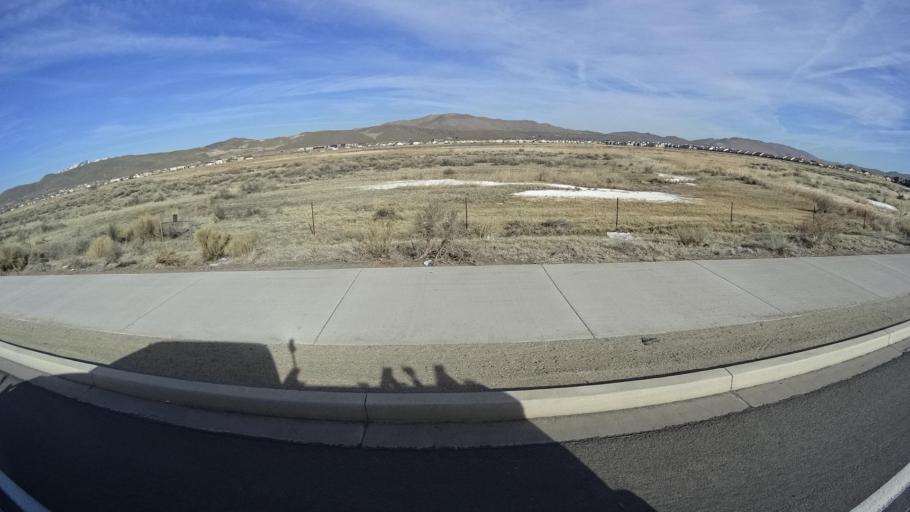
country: US
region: Nevada
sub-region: Washoe County
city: Spanish Springs
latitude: 39.6037
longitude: -119.7073
